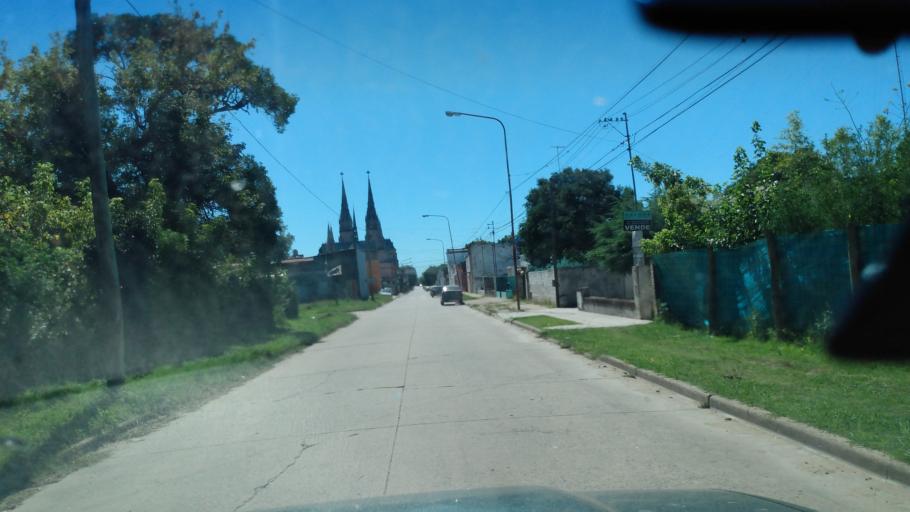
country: AR
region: Buenos Aires
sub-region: Partido de Lujan
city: Lujan
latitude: -34.5698
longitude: -59.1231
